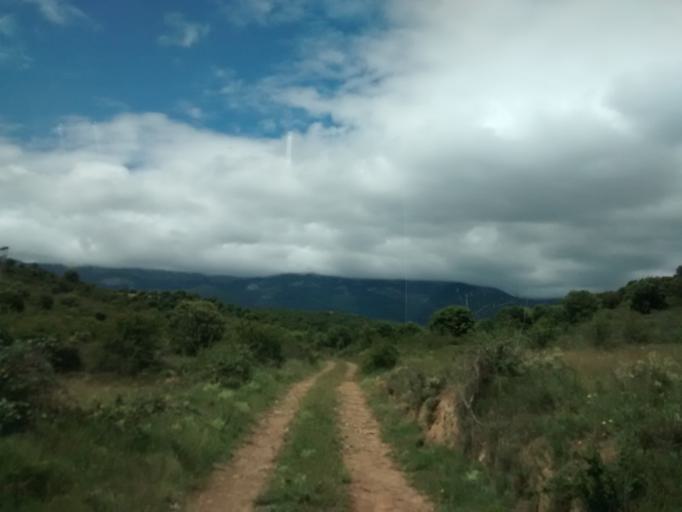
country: ES
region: Aragon
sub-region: Provincia de Zaragoza
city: Lituenigo
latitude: 41.8308
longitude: -1.7456
